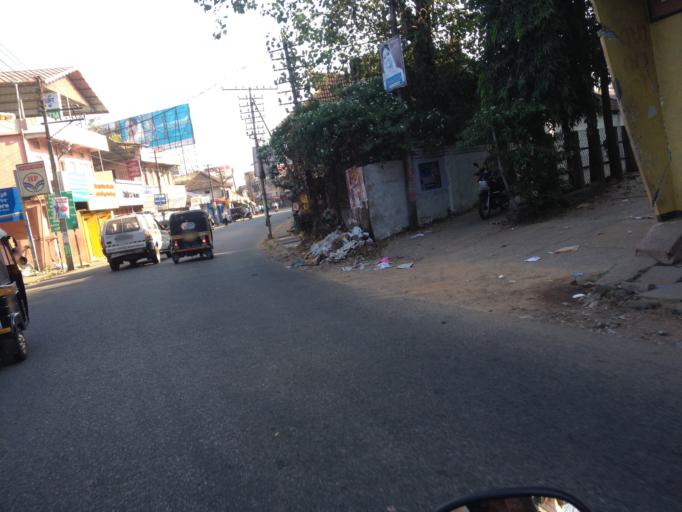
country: IN
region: Kerala
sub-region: Kollam
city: Punalur
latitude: 9.0023
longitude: 76.7731
